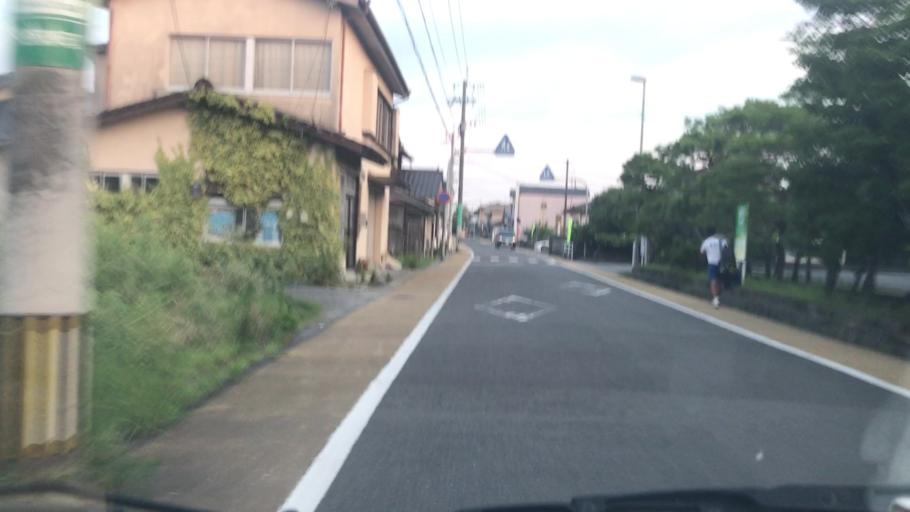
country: JP
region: Saga Prefecture
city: Saga-shi
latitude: 33.2498
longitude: 130.2807
